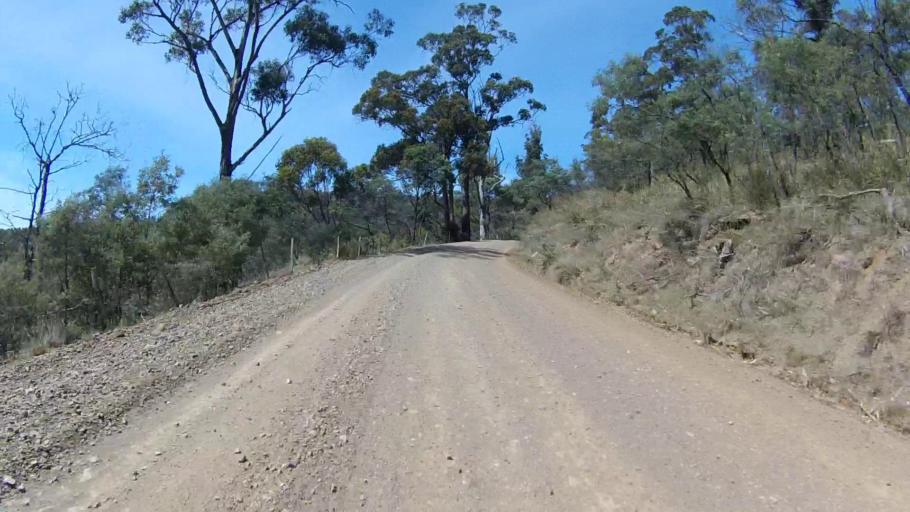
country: AU
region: Tasmania
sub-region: Sorell
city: Sorell
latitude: -42.6497
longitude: 147.7439
